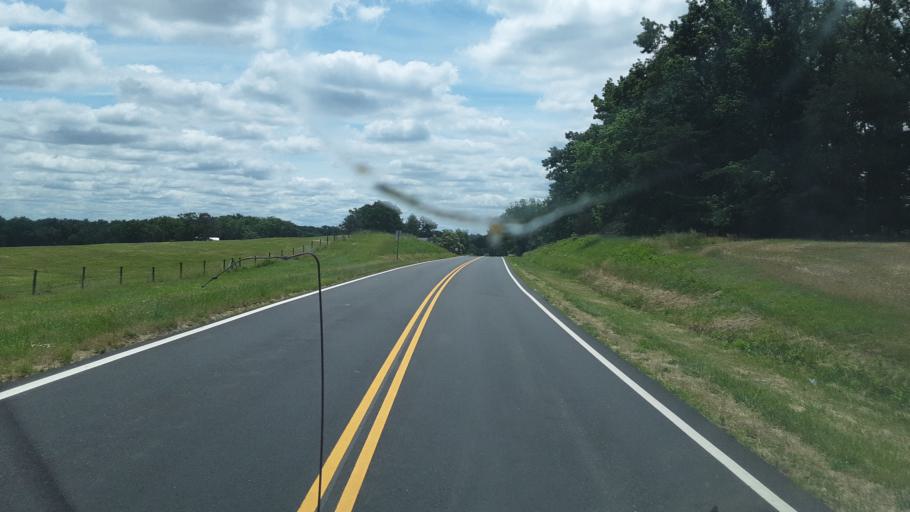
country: US
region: Virginia
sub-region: Pittsylvania County
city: Chatham
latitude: 36.8366
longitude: -79.4432
